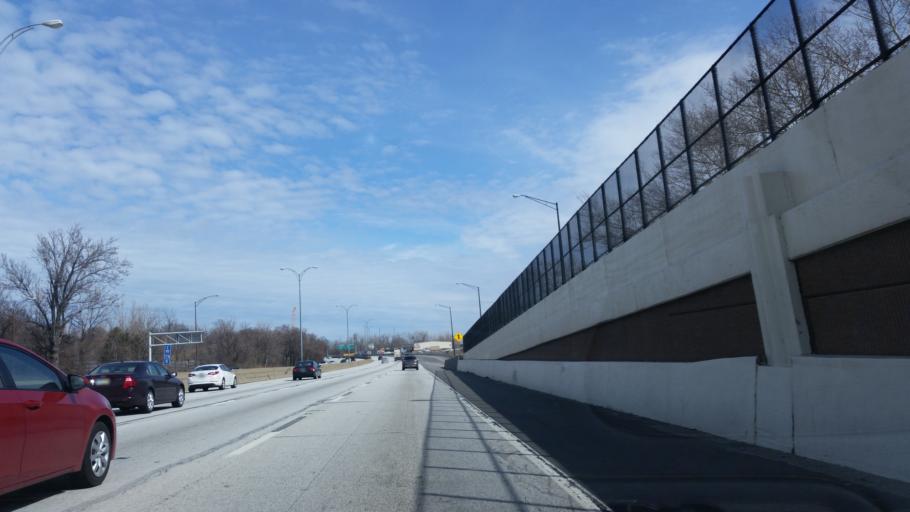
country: US
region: Ohio
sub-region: Cuyahoga County
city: Bratenahl
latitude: 41.5518
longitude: -81.6016
